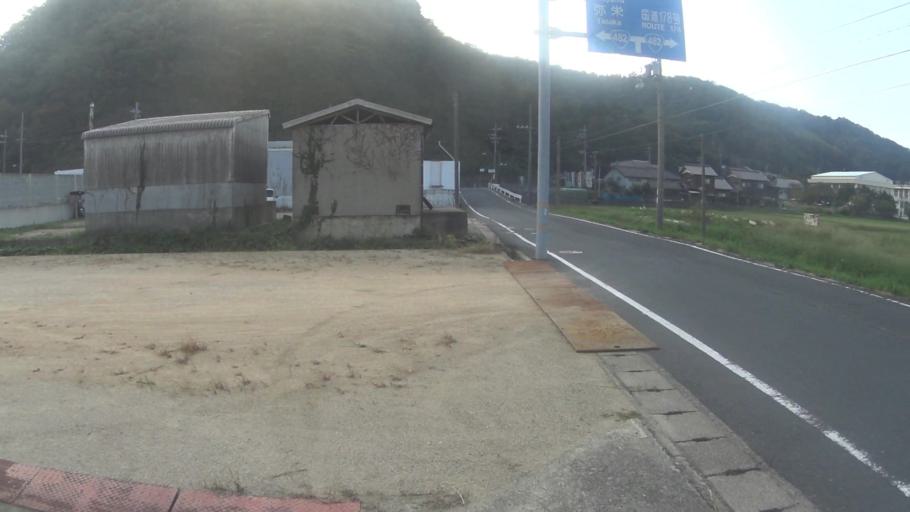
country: JP
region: Kyoto
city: Miyazu
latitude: 35.7291
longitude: 135.0994
